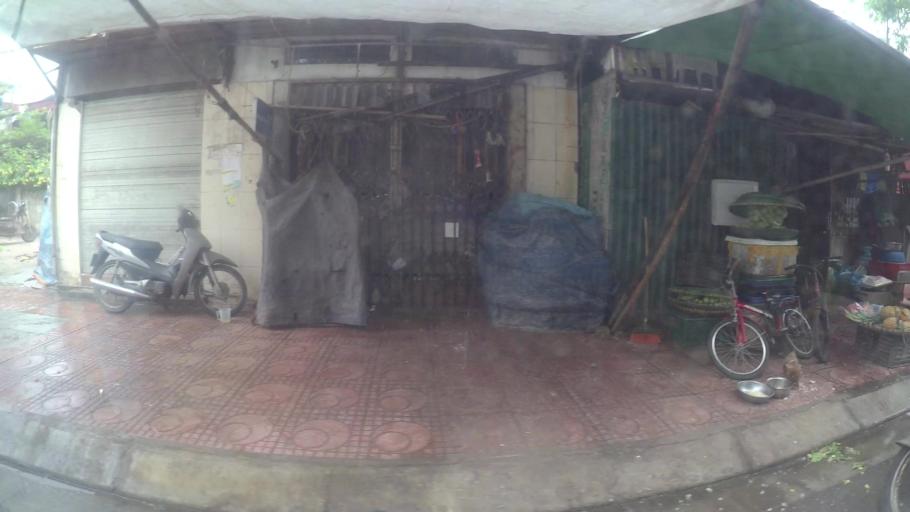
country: VN
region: Ha Noi
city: Hoan Kiem
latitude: 21.0414
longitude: 105.8520
